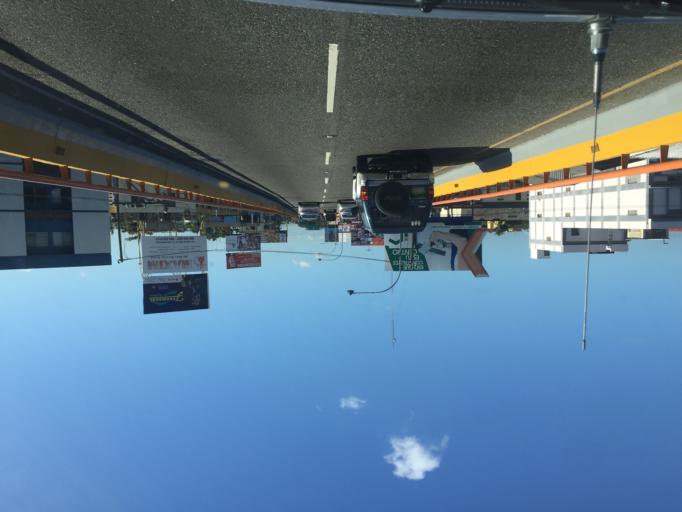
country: DO
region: Nacional
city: San Carlos
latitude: 18.4844
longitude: -69.8906
